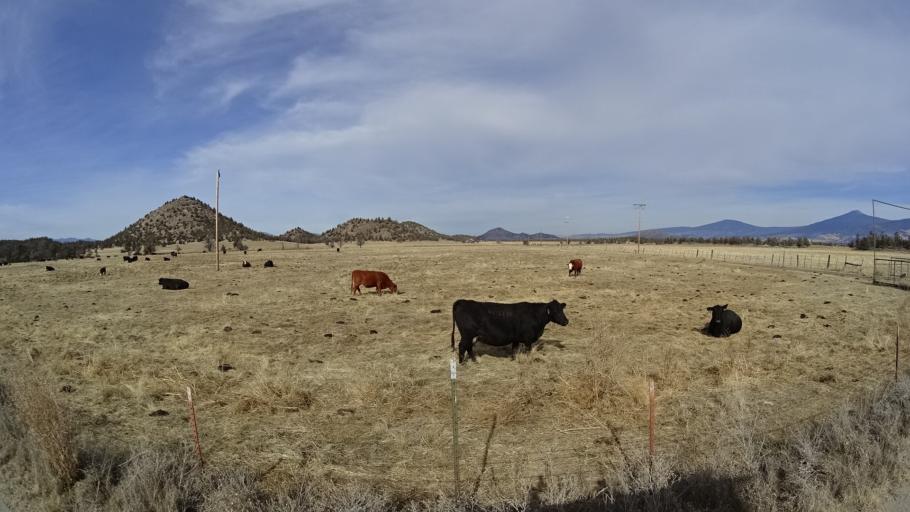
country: US
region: California
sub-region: Siskiyou County
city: Montague
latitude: 41.5948
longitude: -122.4290
